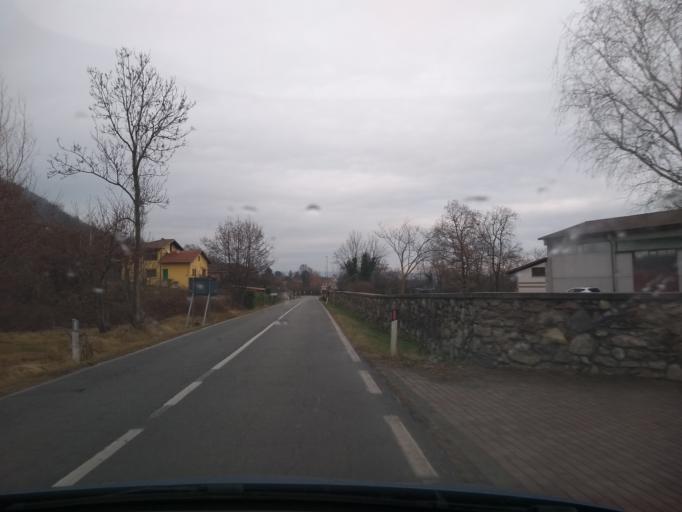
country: IT
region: Piedmont
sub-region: Provincia di Torino
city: Strambinello
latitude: 45.4224
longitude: 7.7724
